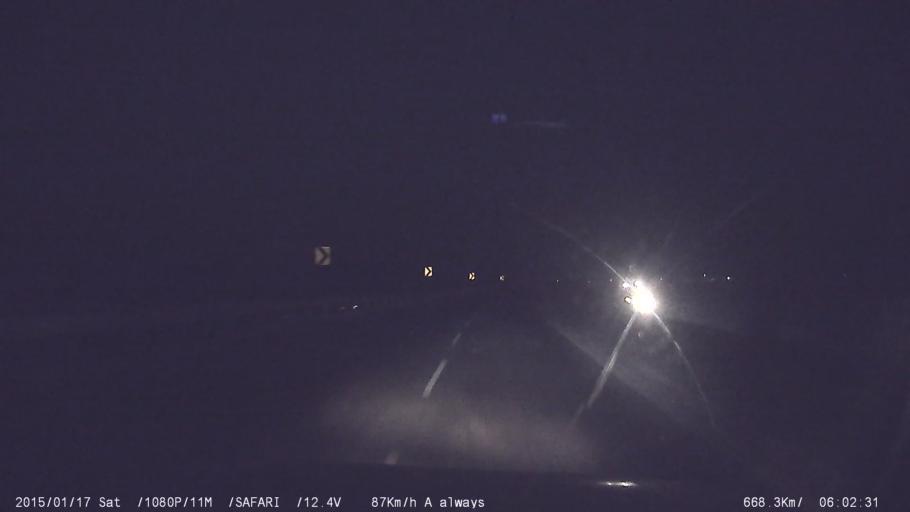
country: IN
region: Tamil Nadu
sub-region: Kancheepuram
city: Kanchipuram
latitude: 12.8902
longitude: 79.5940
